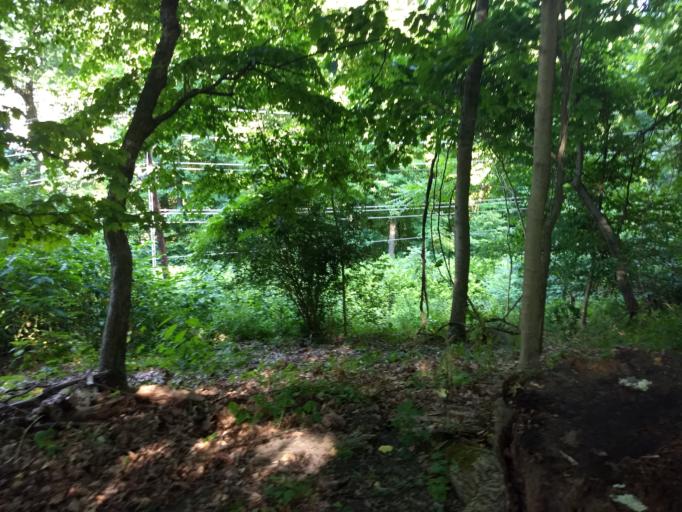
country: US
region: Pennsylvania
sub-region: Westmoreland County
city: Irwin
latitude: 40.3342
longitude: -79.7198
